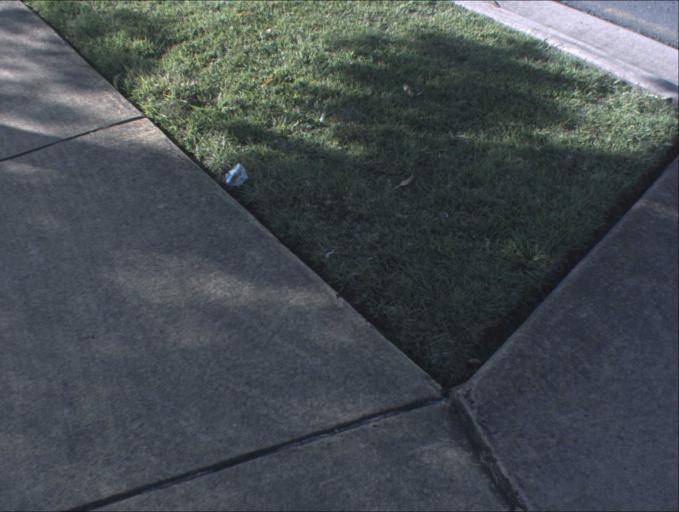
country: AU
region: Queensland
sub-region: Logan
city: Chambers Flat
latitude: -27.7678
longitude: 153.1079
